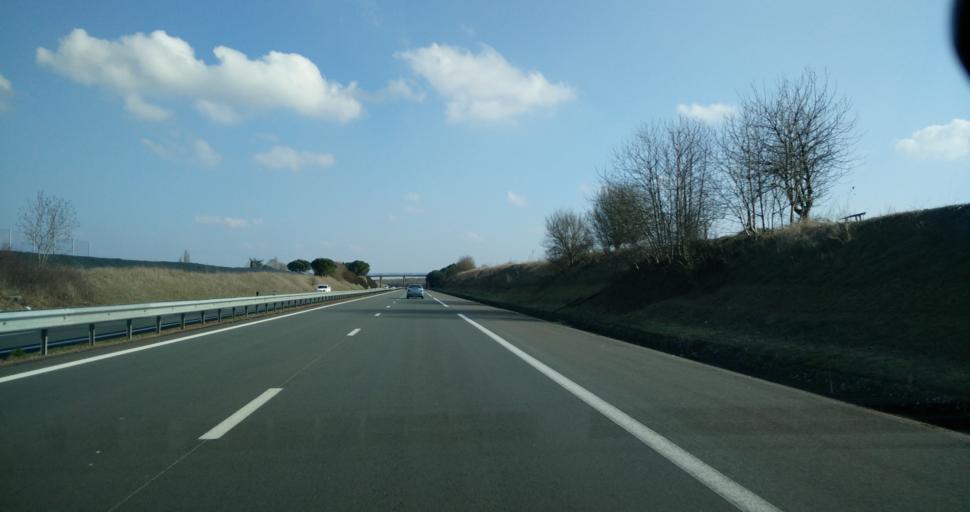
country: FR
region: Poitou-Charentes
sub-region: Departement de la Charente-Maritime
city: Saint-Jean-de-Liversay
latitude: 46.2251
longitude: -0.8650
